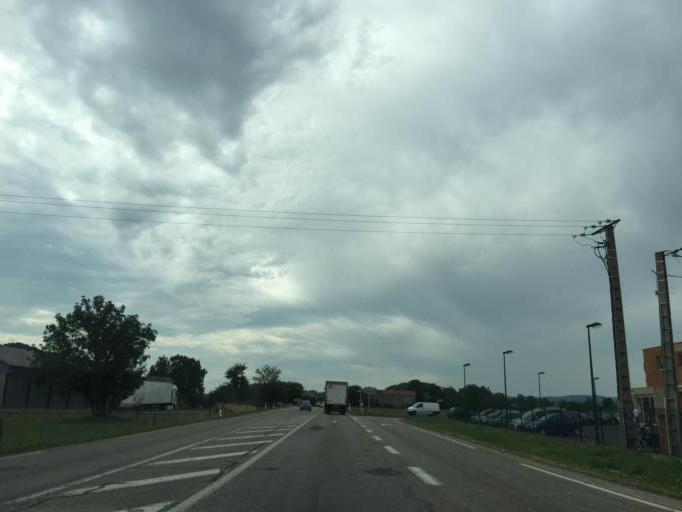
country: FR
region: Auvergne
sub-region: Departement de la Haute-Loire
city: Solignac-sur-Loire
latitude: 44.9638
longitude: 3.8447
